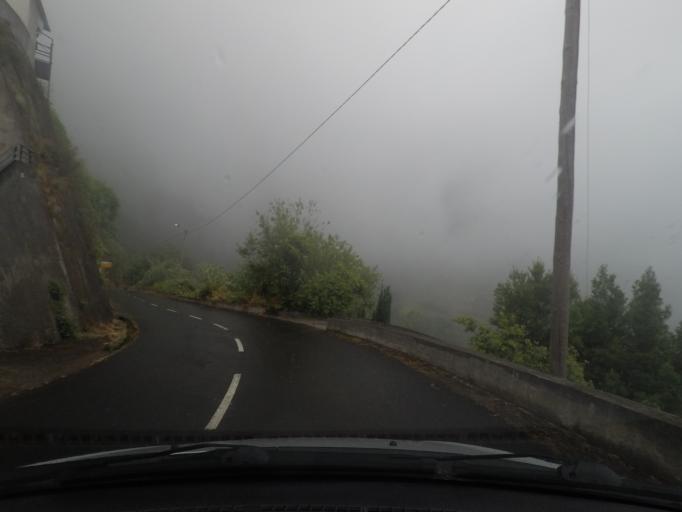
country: PT
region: Madeira
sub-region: Santana
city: Santana
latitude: 32.7737
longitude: -16.8721
